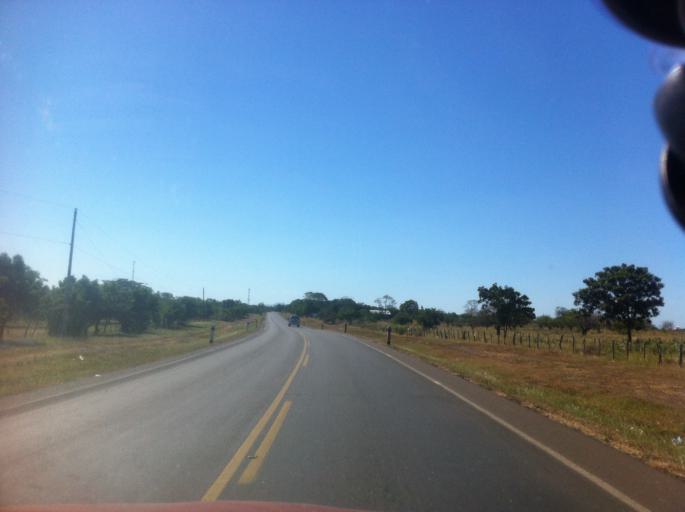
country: NI
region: Managua
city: Tipitapa
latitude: 12.3112
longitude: -86.0394
